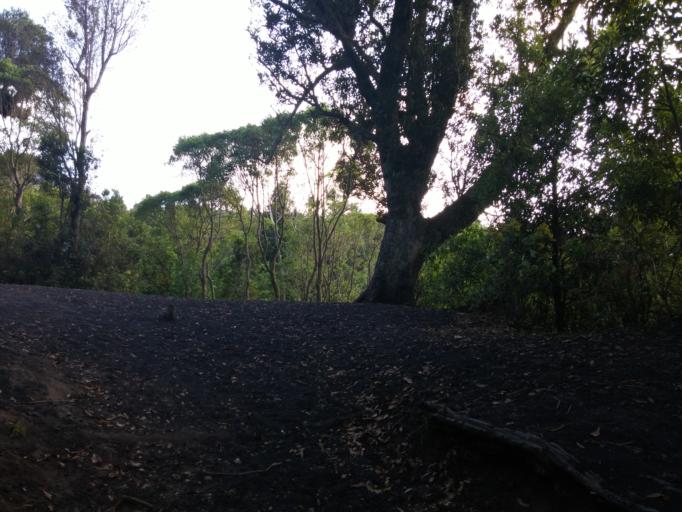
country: GT
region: Escuintla
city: San Vicente Pacaya
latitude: 14.3940
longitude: -90.6005
